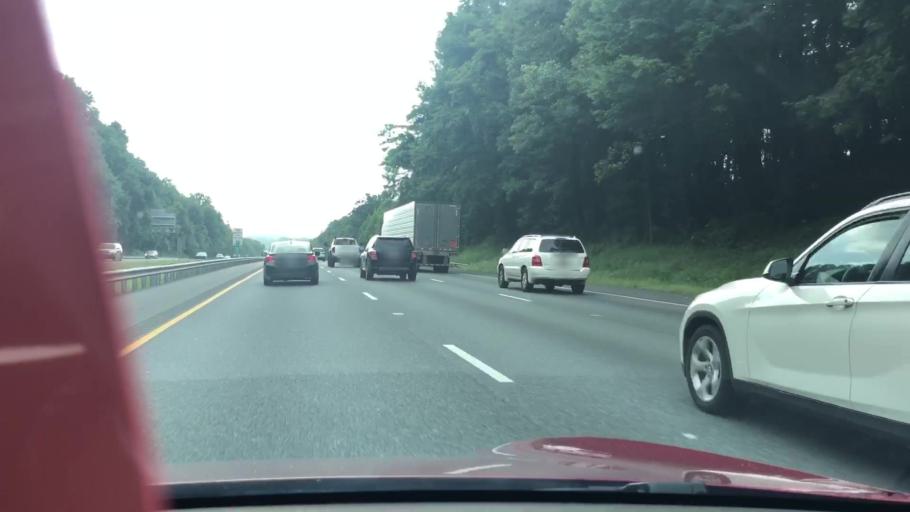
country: US
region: Maryland
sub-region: Harford County
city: Aberdeen
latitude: 39.5618
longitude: -76.1482
